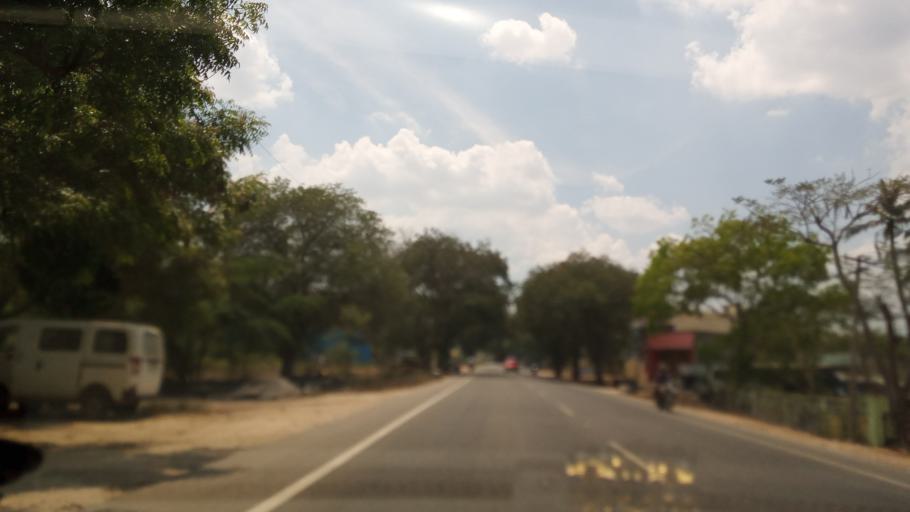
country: IN
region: Tamil Nadu
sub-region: Vellore
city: Walajapet
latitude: 12.9196
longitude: 79.3821
